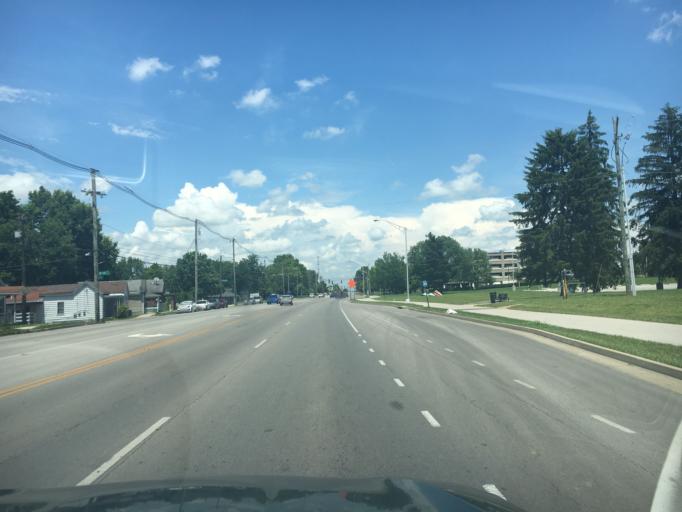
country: US
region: Kentucky
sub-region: Fayette County
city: Mount Vernon
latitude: 38.0620
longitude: -84.5003
